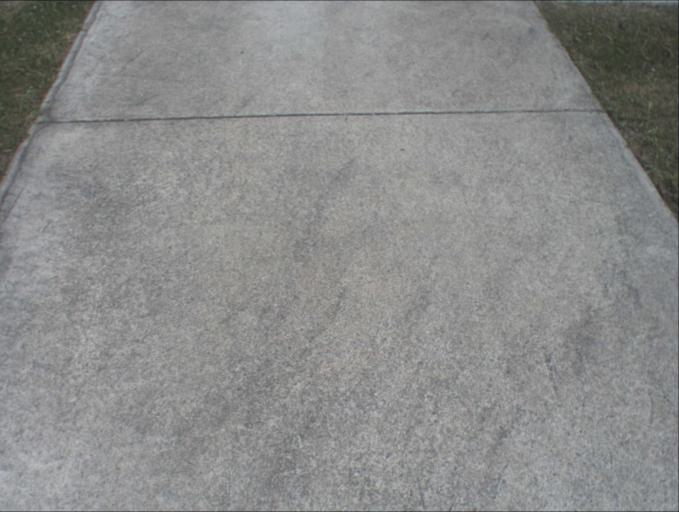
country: AU
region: Queensland
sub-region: Logan
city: Waterford West
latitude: -27.7145
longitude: 153.1593
